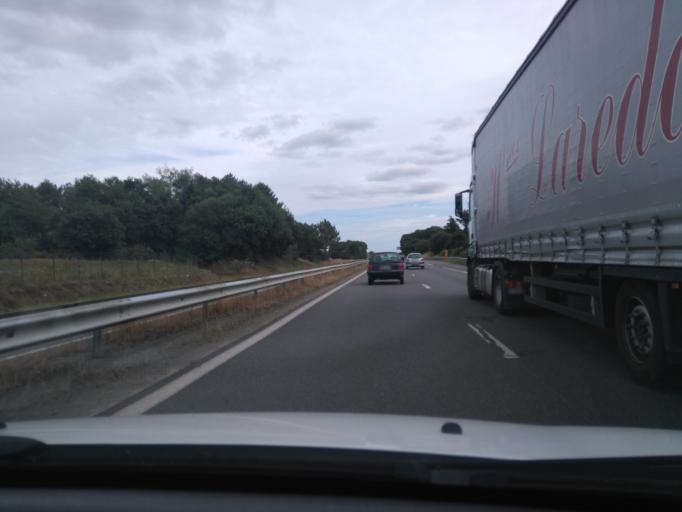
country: FR
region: Brittany
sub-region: Departement des Cotes-d'Armor
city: Plenee-Jugon
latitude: 48.3975
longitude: -2.4045
